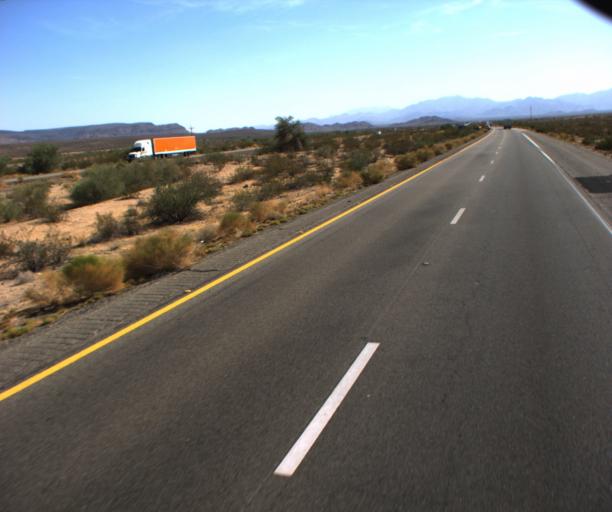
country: US
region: Arizona
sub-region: Mohave County
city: Desert Hills
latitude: 34.7543
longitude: -114.2168
